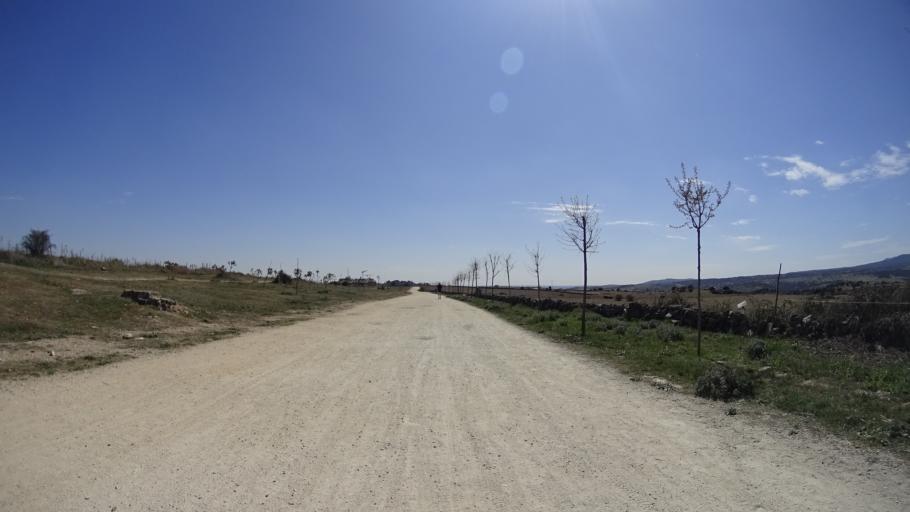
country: ES
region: Madrid
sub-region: Provincia de Madrid
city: Colmenar Viejo
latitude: 40.6592
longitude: -3.7897
